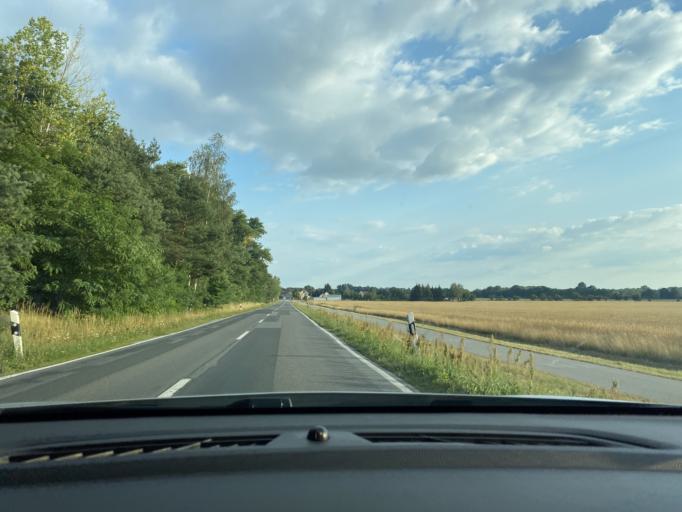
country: DE
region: Saxony
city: Konigswartha
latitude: 51.3344
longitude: 14.3420
